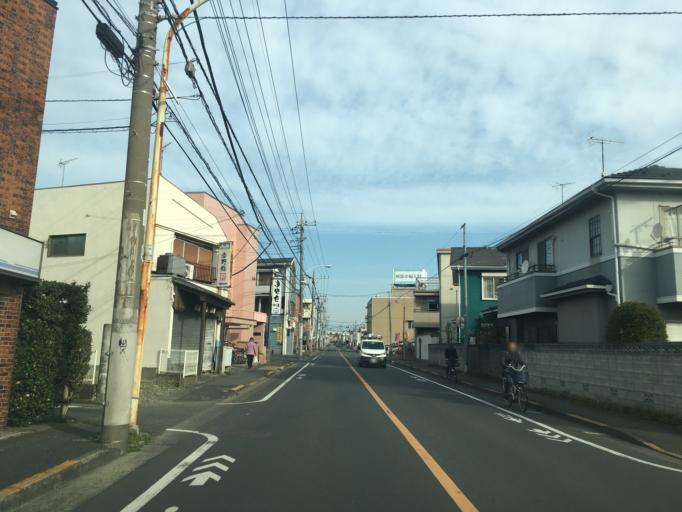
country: JP
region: Tokyo
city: Higashimurayama-shi
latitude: 35.7435
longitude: 139.4299
